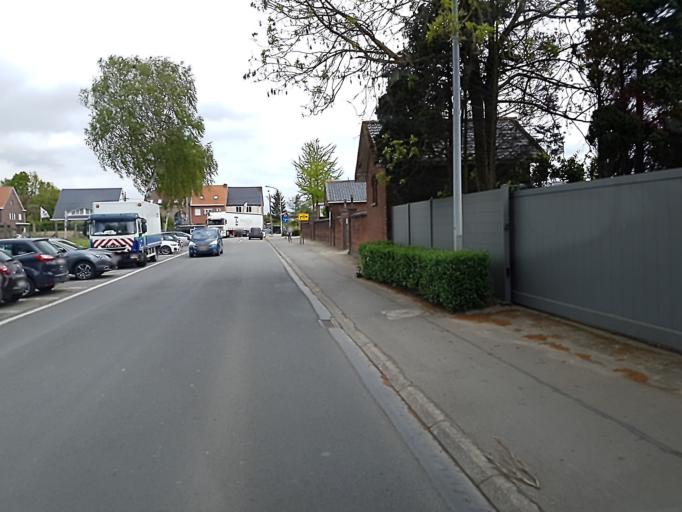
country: BE
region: Flanders
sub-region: Provincie Vlaams-Brabant
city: Londerzeel
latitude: 51.0010
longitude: 4.3072
